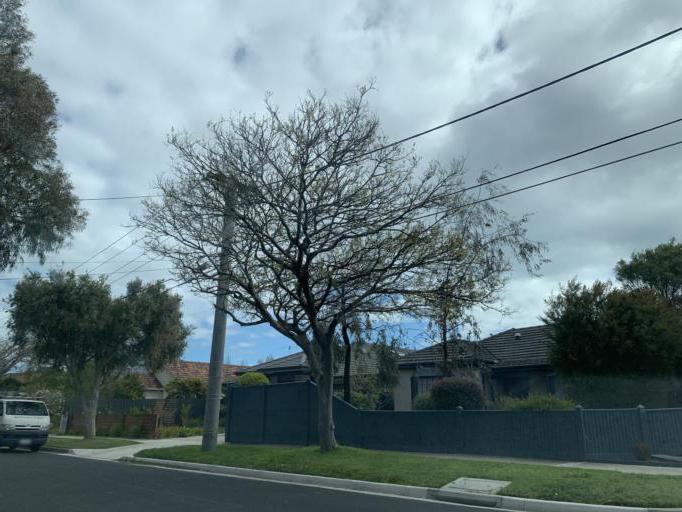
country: AU
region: Victoria
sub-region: Bayside
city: Cheltenham
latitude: -37.9737
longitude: 145.0495
